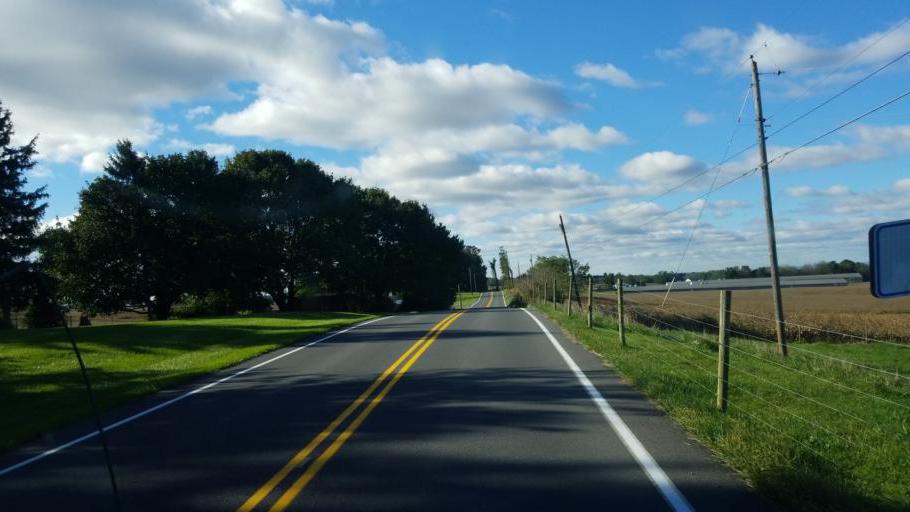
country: US
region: Pennsylvania
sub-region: Franklin County
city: Guilford Siding
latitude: 39.8210
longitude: -77.6404
